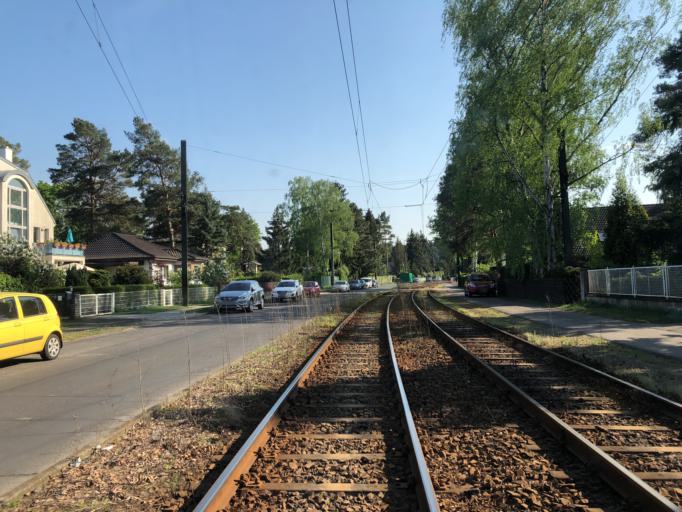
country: DE
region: Berlin
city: Schmockwitz
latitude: 52.3893
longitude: 13.6352
